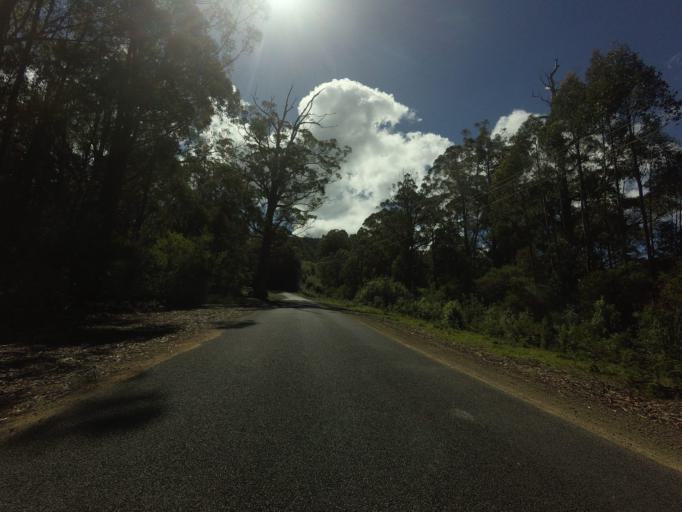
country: AU
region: Tasmania
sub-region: Break O'Day
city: St Helens
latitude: -41.6414
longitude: 148.2428
